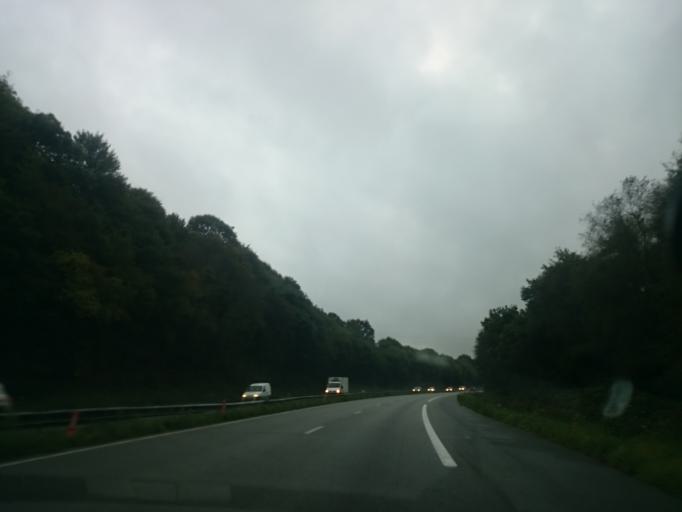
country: FR
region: Brittany
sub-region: Departement du Finistere
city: Chateaulin
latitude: 48.1755
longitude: -4.0435
